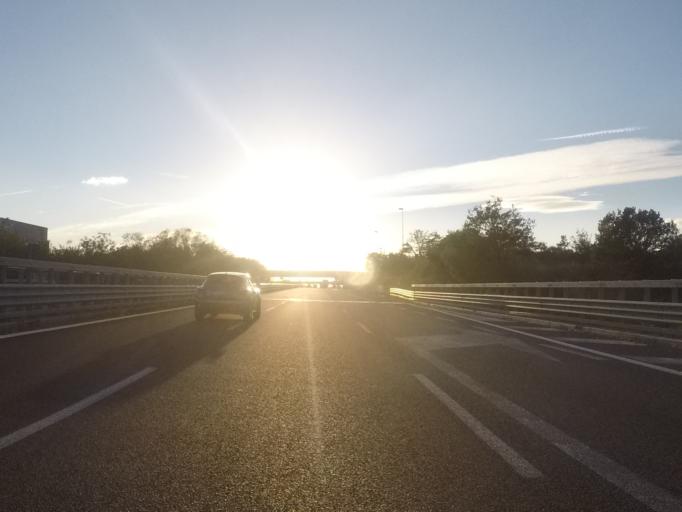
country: IT
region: Campania
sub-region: Provincia di Salerno
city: Quadrivio
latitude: 40.6074
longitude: 15.1228
